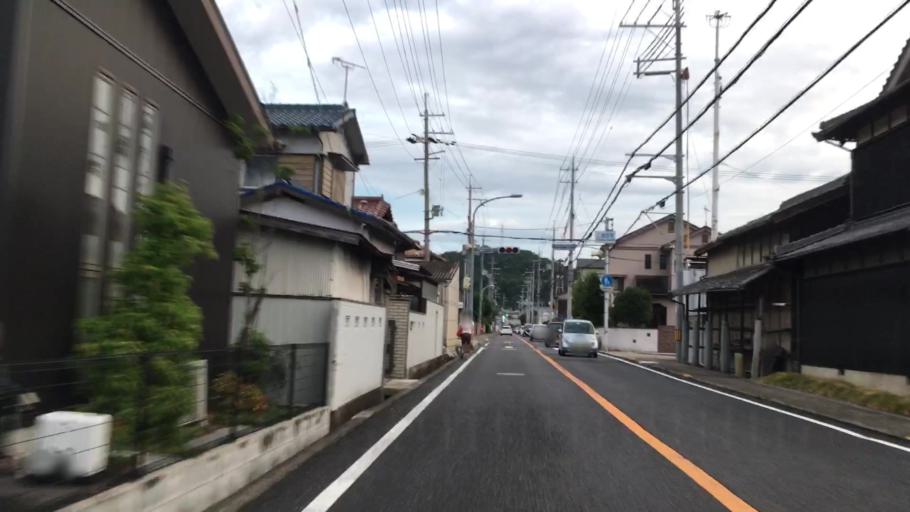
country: JP
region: Hyogo
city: Himeji
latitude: 34.8839
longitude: 134.7294
